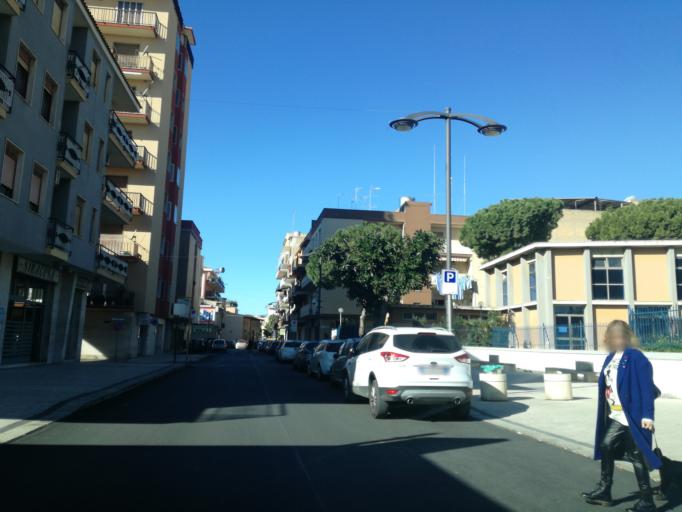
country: IT
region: Sicily
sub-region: Provincia di Caltanissetta
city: Gela
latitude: 37.0739
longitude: 14.2298
